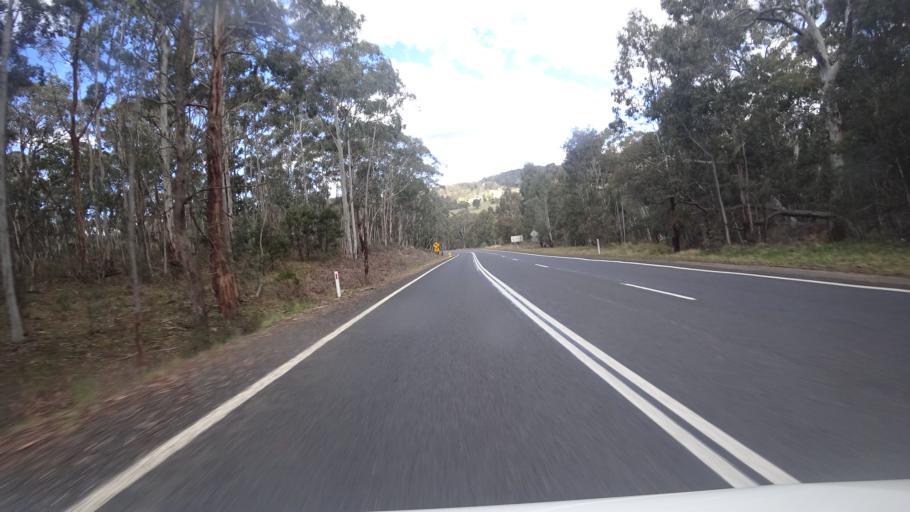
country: AU
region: New South Wales
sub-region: Oberon
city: Oberon
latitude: -33.7109
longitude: 150.0168
